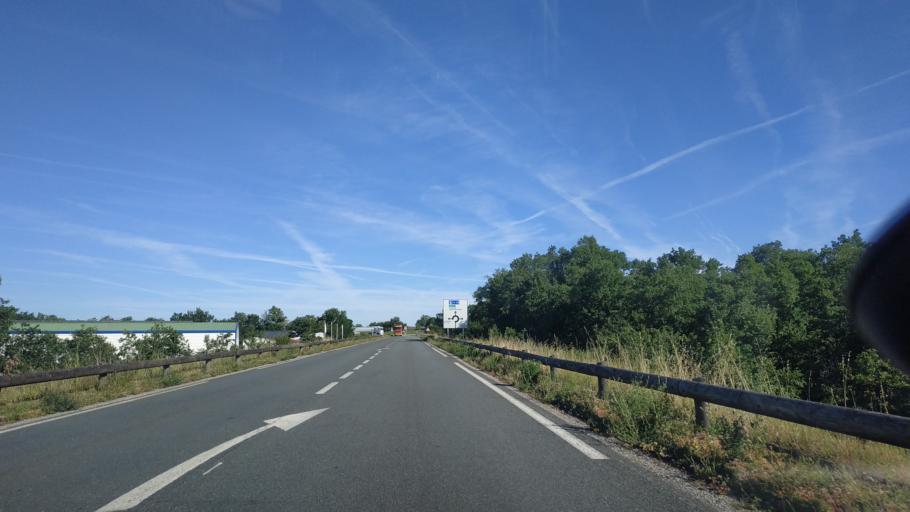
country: FR
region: Midi-Pyrenees
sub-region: Departement du Lot
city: Lacapelle-Marival
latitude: 44.6546
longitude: 1.8544
